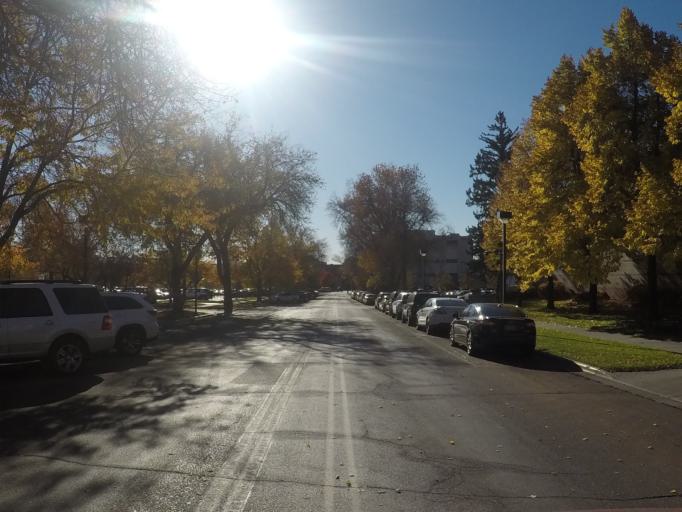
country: US
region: Montana
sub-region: Yellowstone County
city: Billings
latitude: 45.7918
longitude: -108.5153
